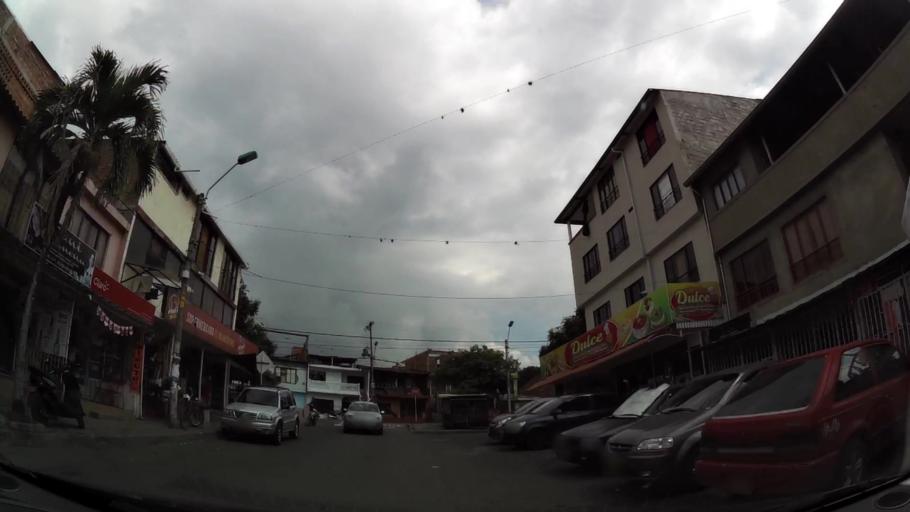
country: CO
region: Valle del Cauca
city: Cali
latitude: 3.4953
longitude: -76.4875
